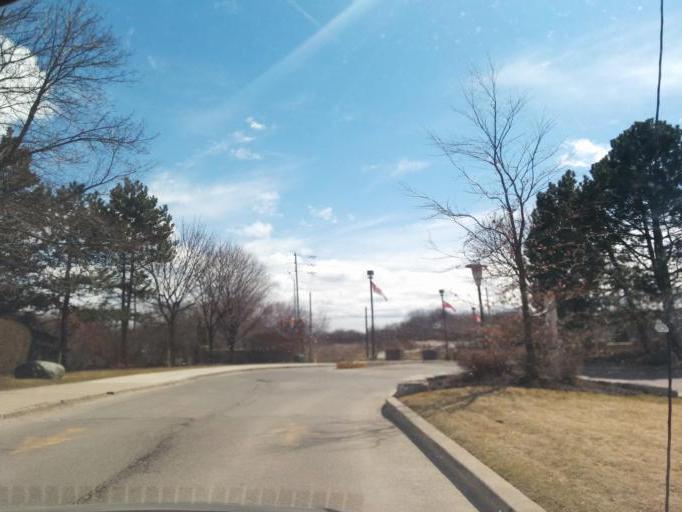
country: CA
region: Ontario
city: Etobicoke
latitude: 43.5885
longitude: -79.5480
